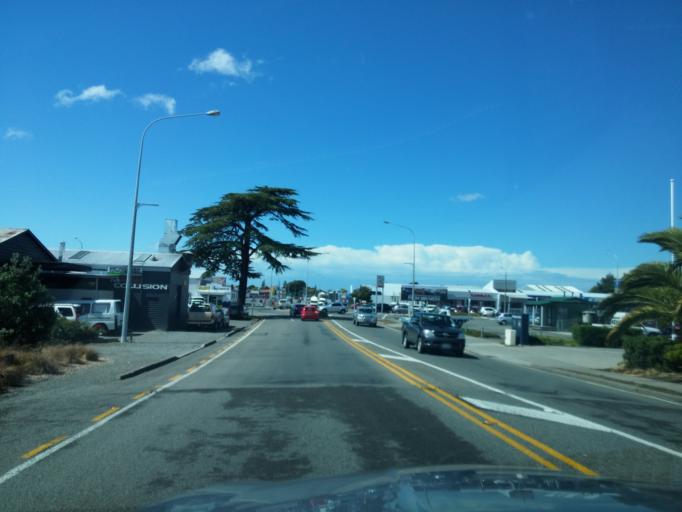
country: NZ
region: Marlborough
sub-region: Marlborough District
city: Blenheim
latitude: -41.5082
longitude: 173.9546
